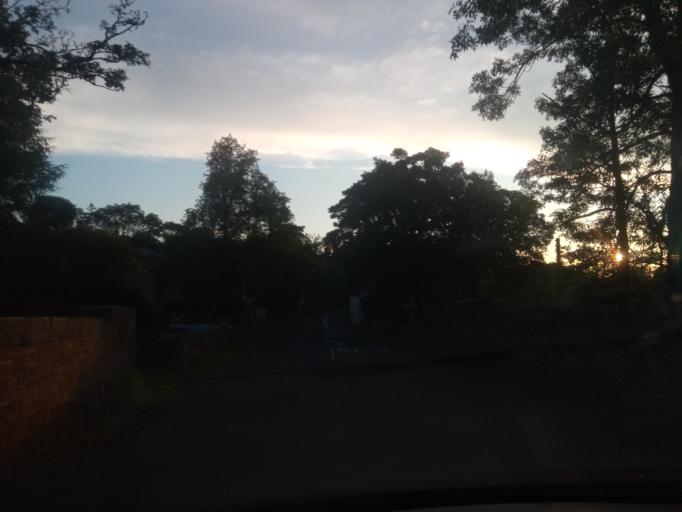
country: GB
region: England
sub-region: Northumberland
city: Bardon Mill
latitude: 54.8062
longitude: -2.3768
